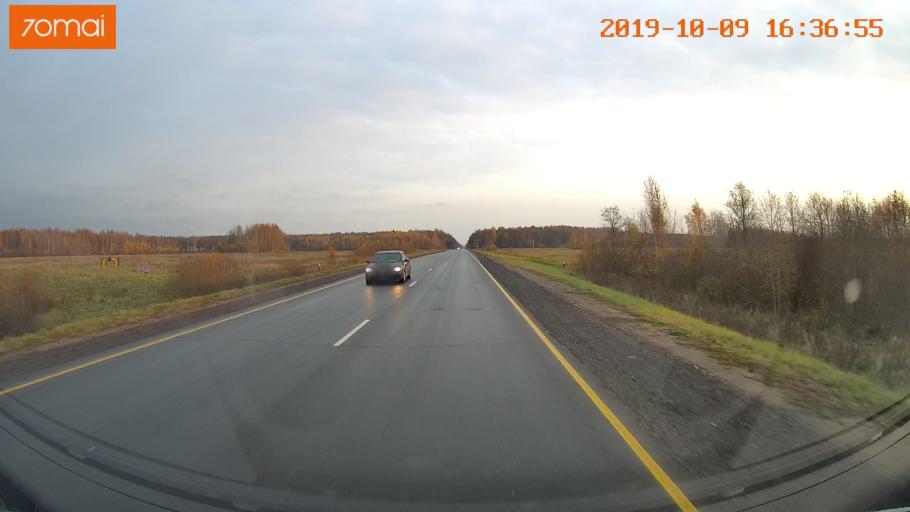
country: RU
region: Kostroma
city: Volgorechensk
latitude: 57.5346
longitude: 41.0183
